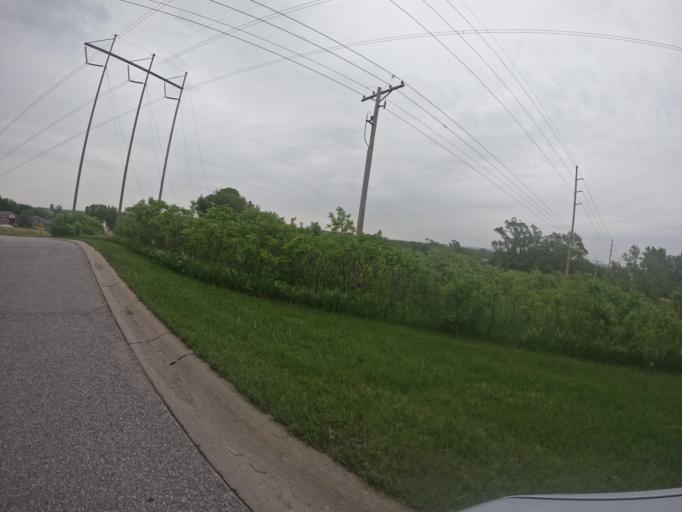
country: US
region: Nebraska
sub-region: Sarpy County
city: Offutt Air Force Base
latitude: 41.0457
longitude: -95.9588
